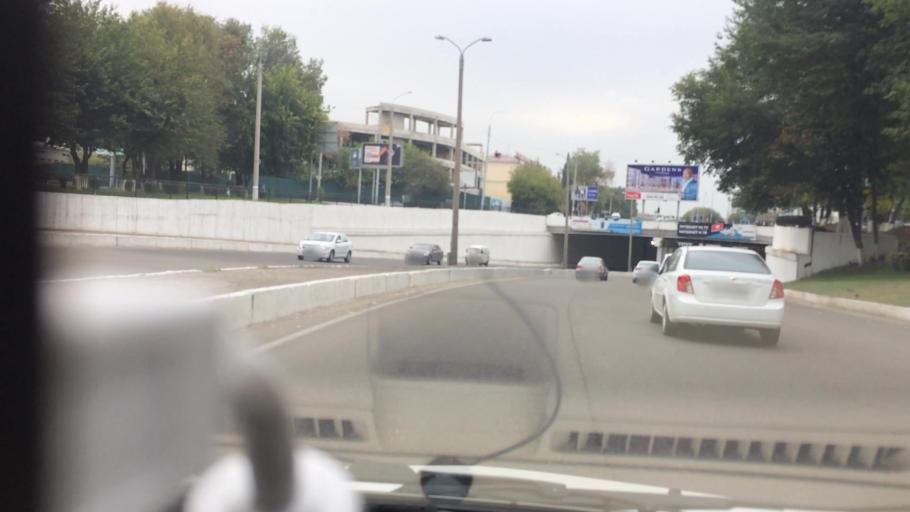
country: UZ
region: Toshkent Shahri
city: Tashkent
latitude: 41.2903
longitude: 69.2831
